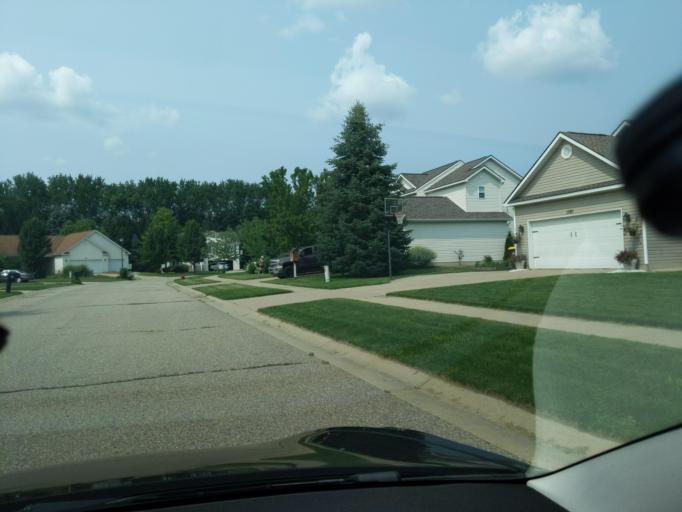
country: US
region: Michigan
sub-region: Ingham County
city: Holt
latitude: 42.6281
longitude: -84.5596
